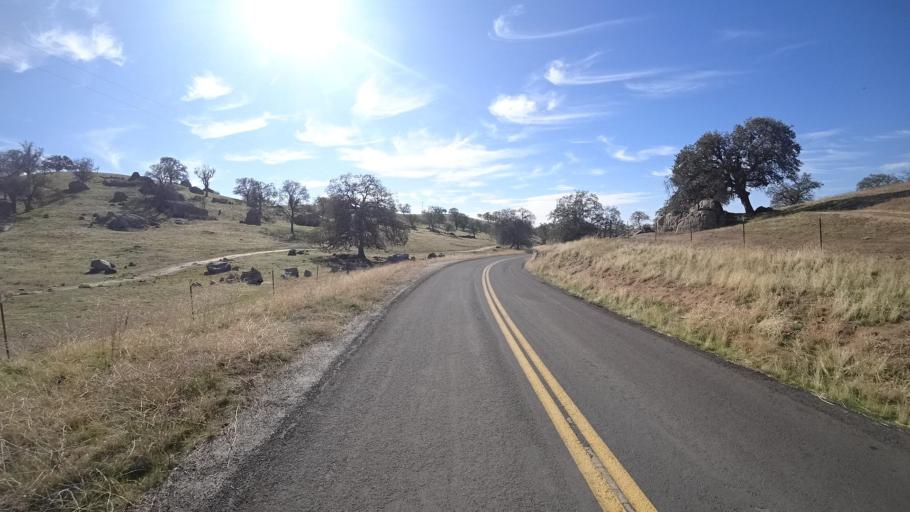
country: US
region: California
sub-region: Kern County
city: Oildale
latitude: 35.6255
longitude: -118.8473
